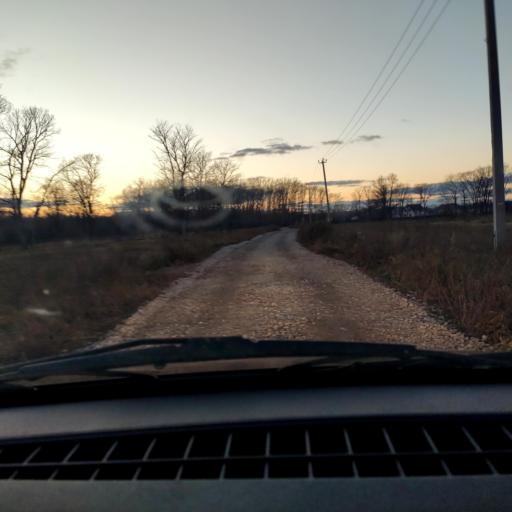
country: RU
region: Bashkortostan
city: Ufa
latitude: 54.6468
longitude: 55.9036
